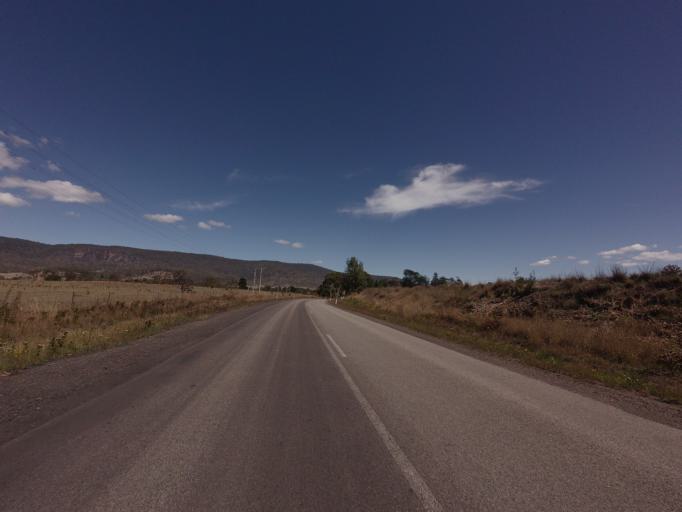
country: AU
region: Tasmania
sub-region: Break O'Day
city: St Helens
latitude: -41.6319
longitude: 147.9850
